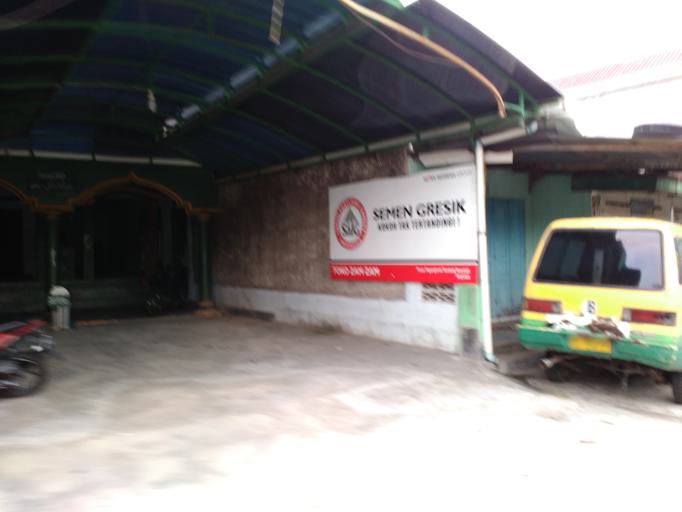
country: ID
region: Central Java
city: Boyolali
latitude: -7.5819
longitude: 110.5964
